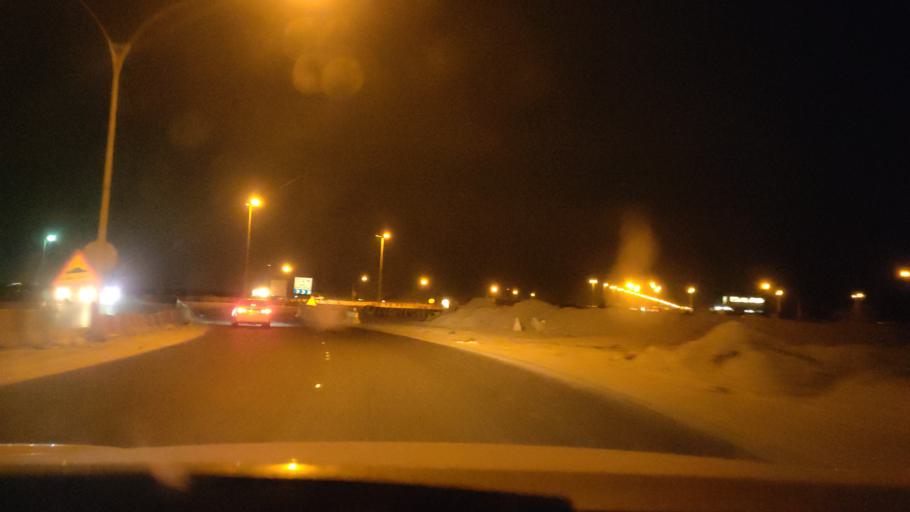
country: KW
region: Al Ahmadi
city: Al Ahmadi
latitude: 28.9535
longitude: 48.1184
